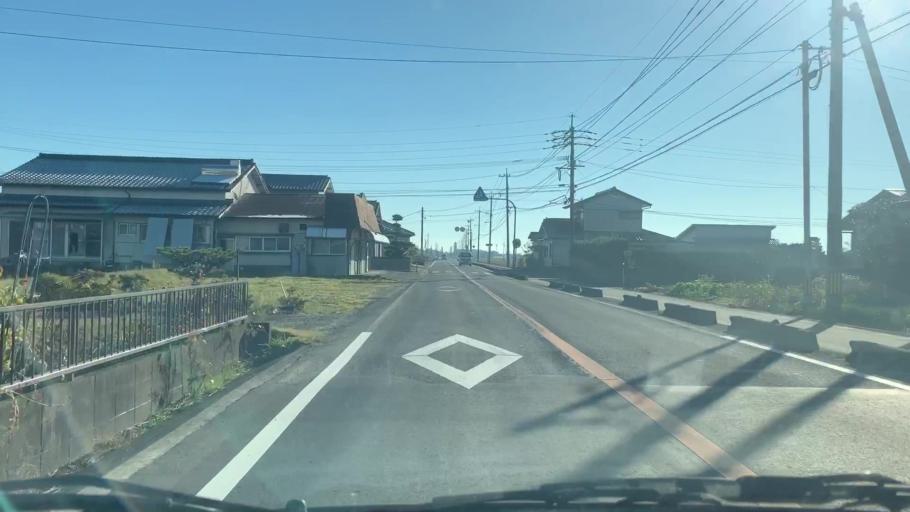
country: JP
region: Saga Prefecture
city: Kashima
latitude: 33.1929
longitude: 130.1215
